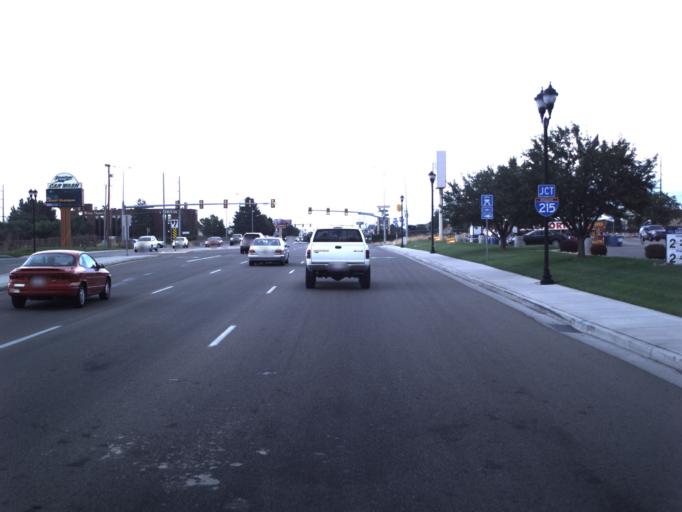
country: US
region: Utah
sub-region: Salt Lake County
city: Midvale
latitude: 40.6298
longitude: -111.8896
